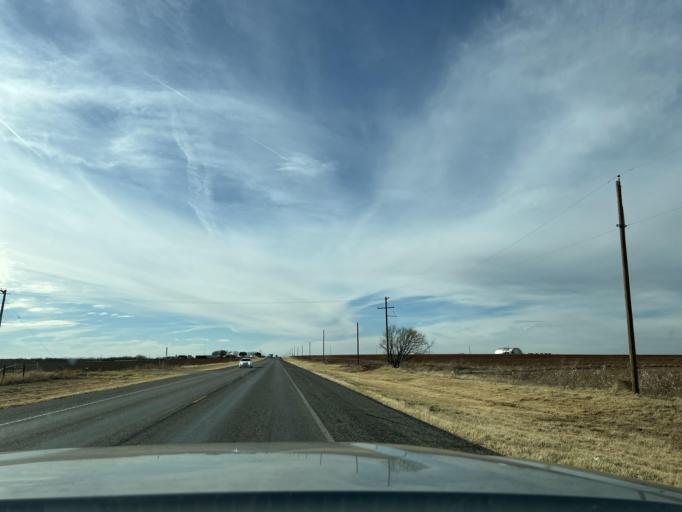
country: US
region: Texas
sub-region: Jones County
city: Anson
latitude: 32.7520
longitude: -99.9392
